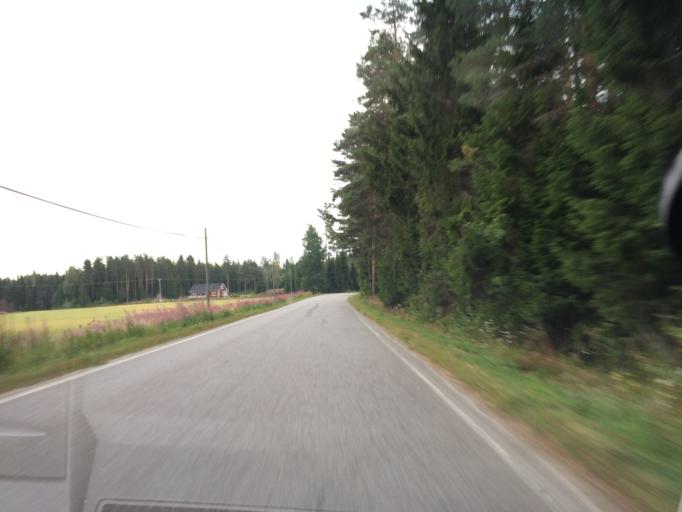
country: FI
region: Haeme
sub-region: Haemeenlinna
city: Tuulos
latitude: 61.1989
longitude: 24.7378
